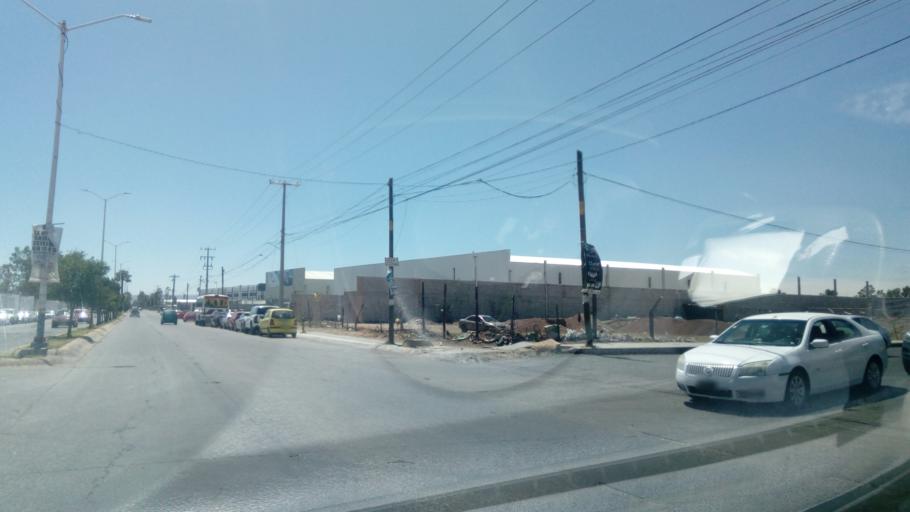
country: MX
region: Durango
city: Victoria de Durango
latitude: 24.0380
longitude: -104.6077
